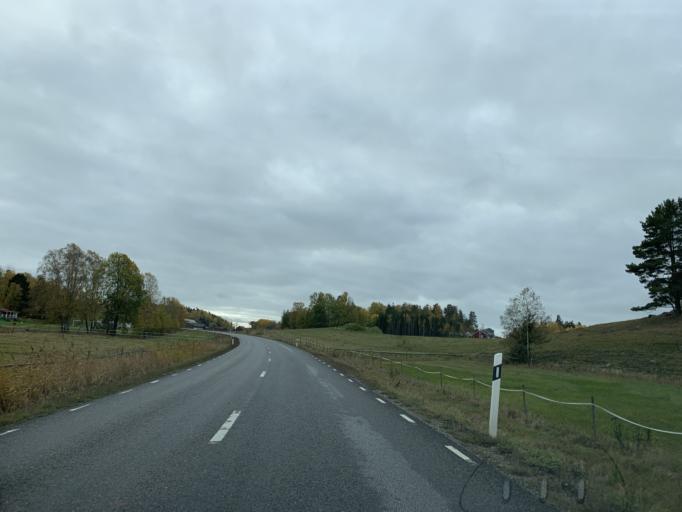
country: SE
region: Stockholm
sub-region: Nynashamns Kommun
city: Osmo
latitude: 59.0245
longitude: 17.7974
